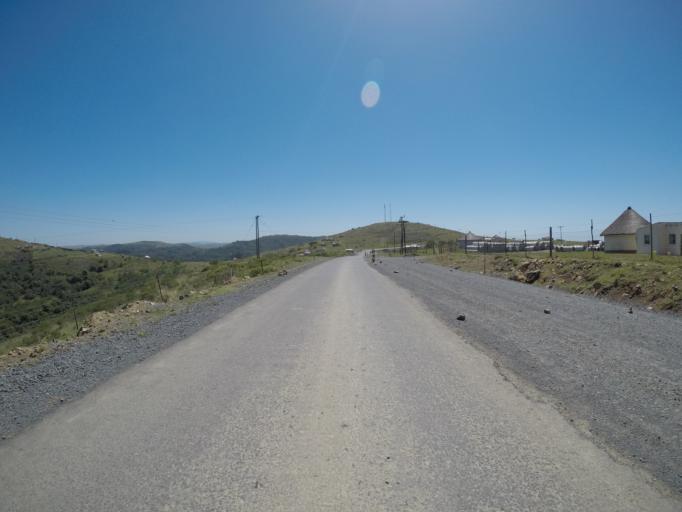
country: ZA
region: Eastern Cape
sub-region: OR Tambo District Municipality
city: Libode
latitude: -32.0030
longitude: 29.1160
